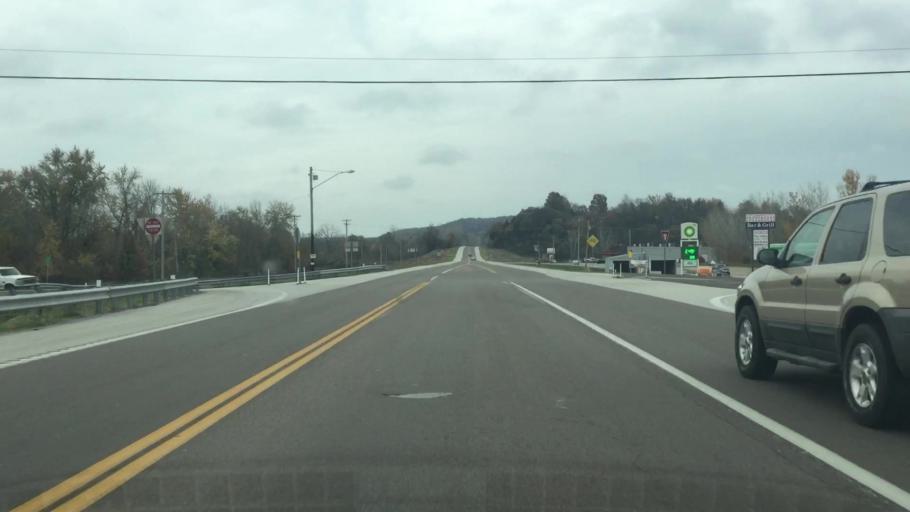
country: US
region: Missouri
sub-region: Gasconade County
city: Hermann
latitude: 38.7285
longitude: -91.4461
